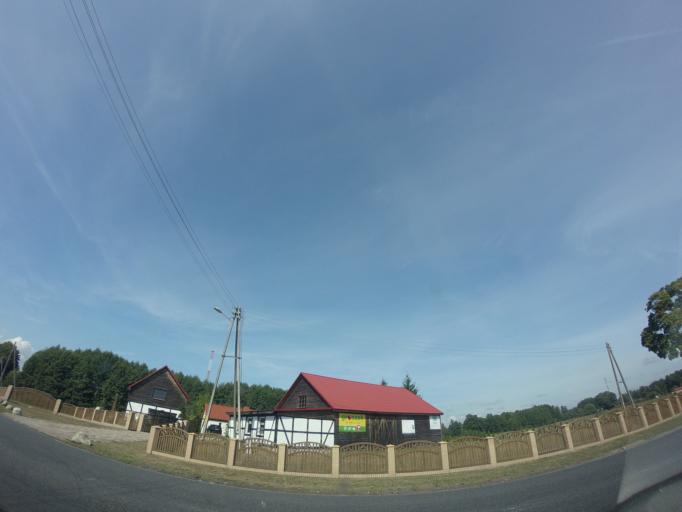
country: PL
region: Lubusz
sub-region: Powiat strzelecko-drezdenecki
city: Stare Kurowo
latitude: 52.7663
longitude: 15.7142
